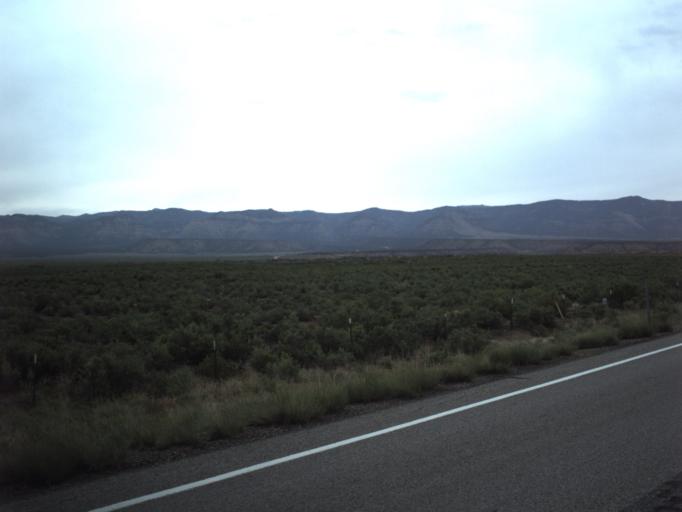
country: US
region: Utah
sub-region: Carbon County
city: East Carbon City
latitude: 39.5320
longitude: -110.5448
